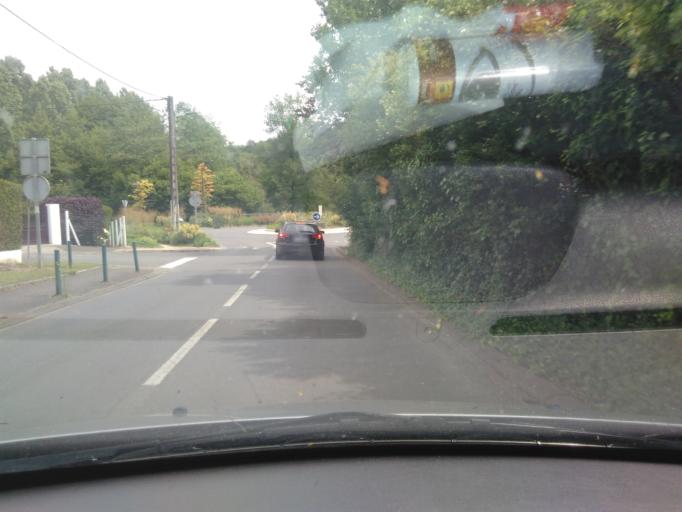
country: FR
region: Centre
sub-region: Departement d'Indre-et-Loire
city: Amboise
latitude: 47.4048
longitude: 1.0022
